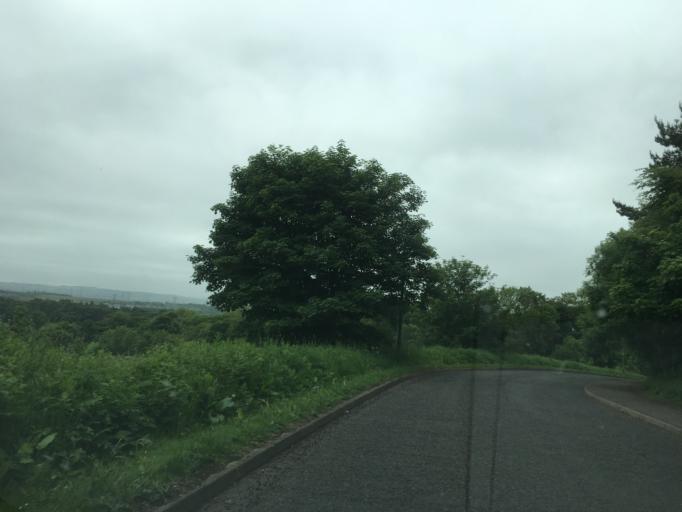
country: GB
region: Scotland
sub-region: Midlothian
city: Loanhead
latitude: 55.9019
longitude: -3.1894
